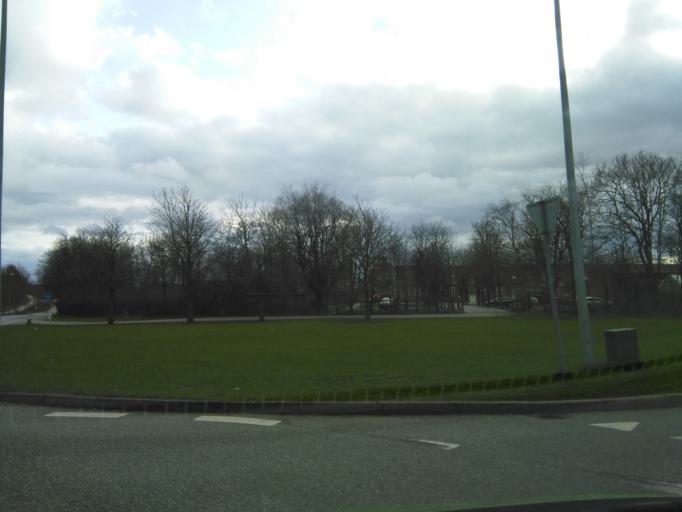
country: DK
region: Central Jutland
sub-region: Arhus Kommune
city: Stavtrup
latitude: 56.1753
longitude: 10.1193
